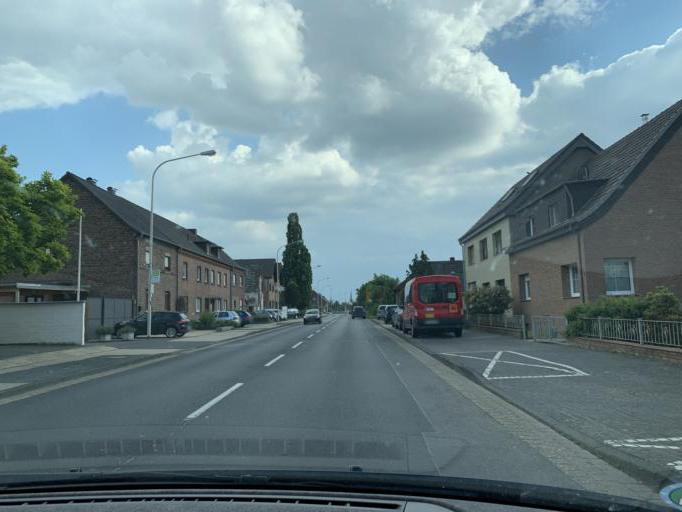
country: DE
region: North Rhine-Westphalia
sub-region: Regierungsbezirk Koln
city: Weilerswist
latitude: 50.7500
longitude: 6.8378
